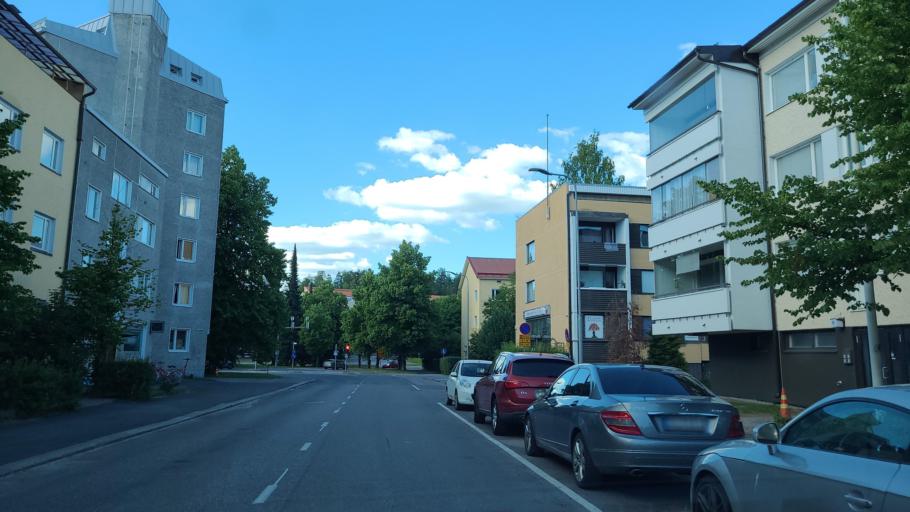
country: FI
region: Central Finland
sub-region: Jyvaeskylae
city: Jyvaeskylae
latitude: 62.2496
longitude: 25.7440
